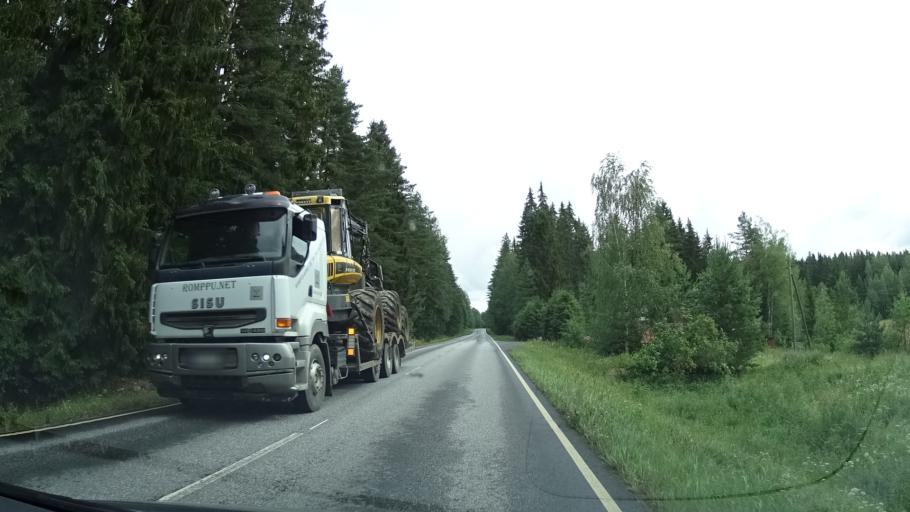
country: FI
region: Haeme
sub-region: Forssa
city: Humppila
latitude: 61.0978
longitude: 23.3346
